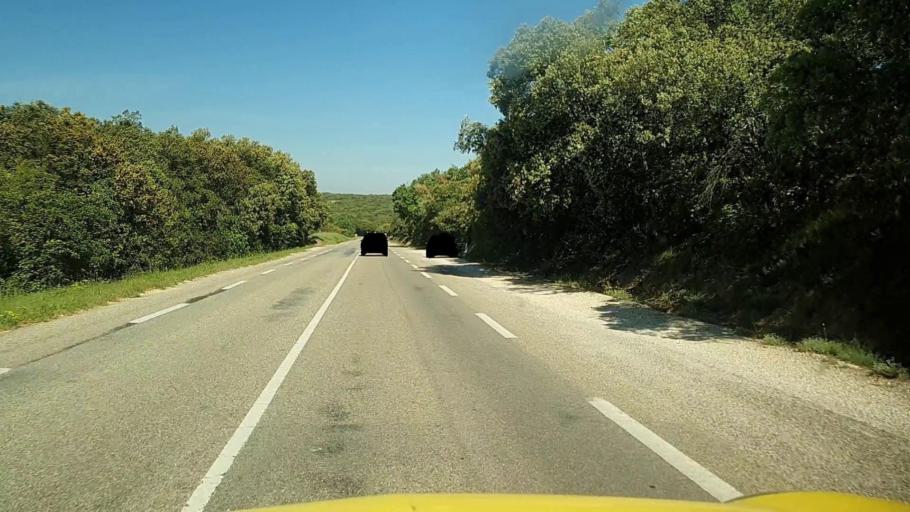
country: FR
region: Languedoc-Roussillon
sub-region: Departement du Gard
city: Poulx
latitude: 43.9158
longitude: 4.3928
